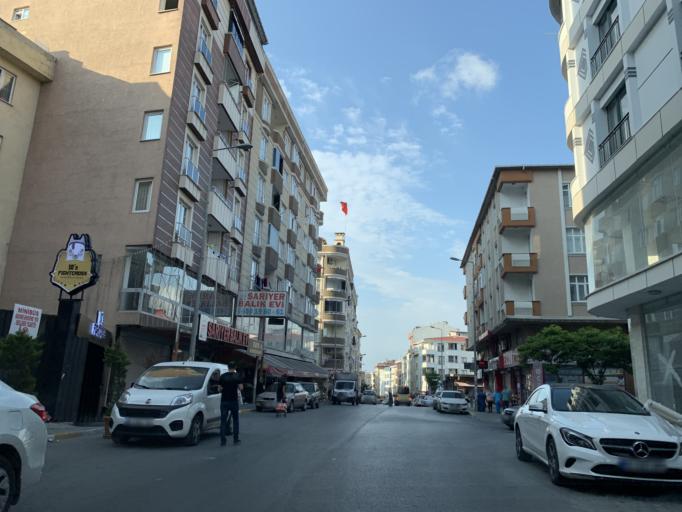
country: TR
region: Istanbul
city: Esenyurt
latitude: 41.0427
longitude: 28.6771
